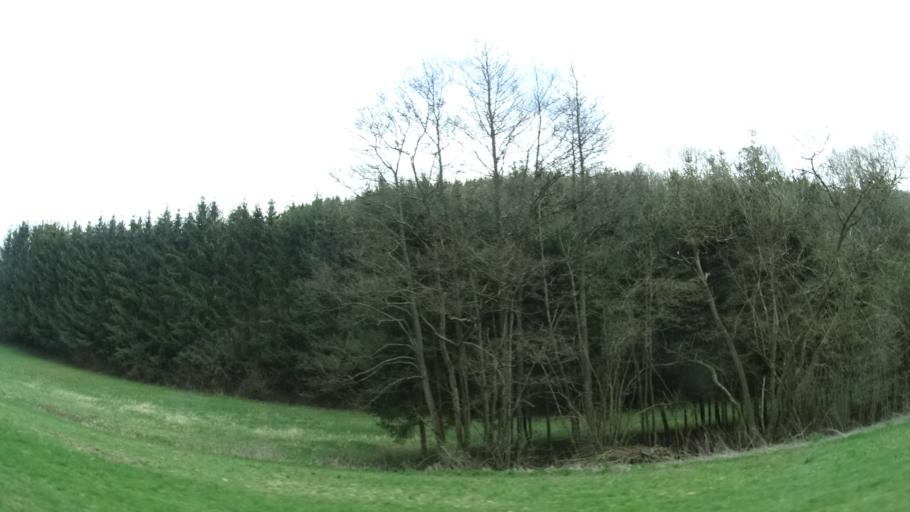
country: DE
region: Rheinland-Pfalz
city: Schwarzerden
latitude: 49.8466
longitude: 7.5101
